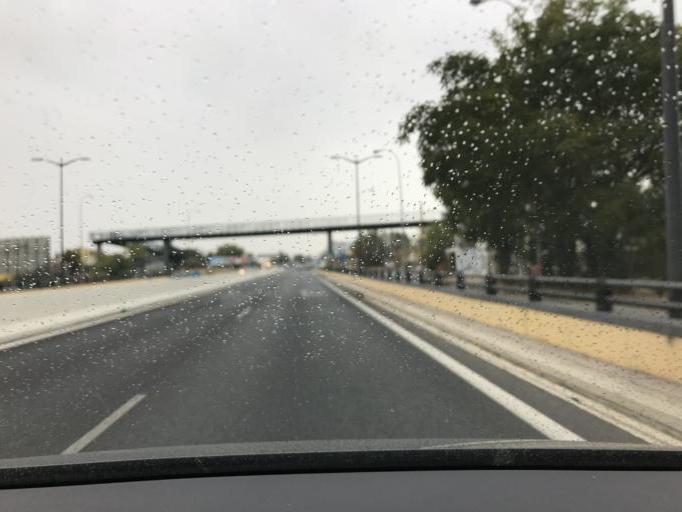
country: ES
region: Andalusia
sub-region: Provincia de Granada
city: Atarfe
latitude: 37.1926
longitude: -3.7170
